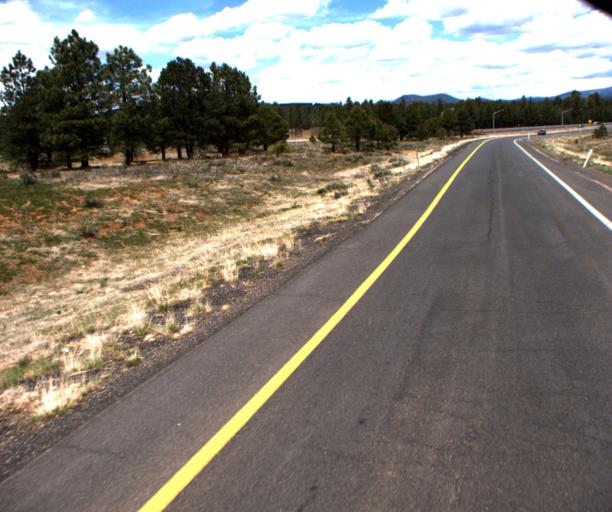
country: US
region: Arizona
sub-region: Coconino County
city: Kachina Village
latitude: 35.1406
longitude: -111.6833
